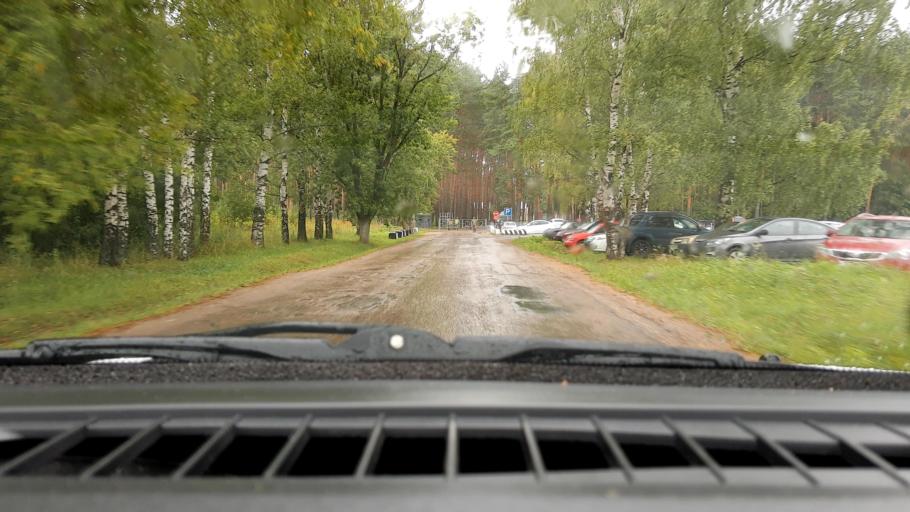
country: RU
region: Nizjnij Novgorod
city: Babino
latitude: 56.1428
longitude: 43.6506
